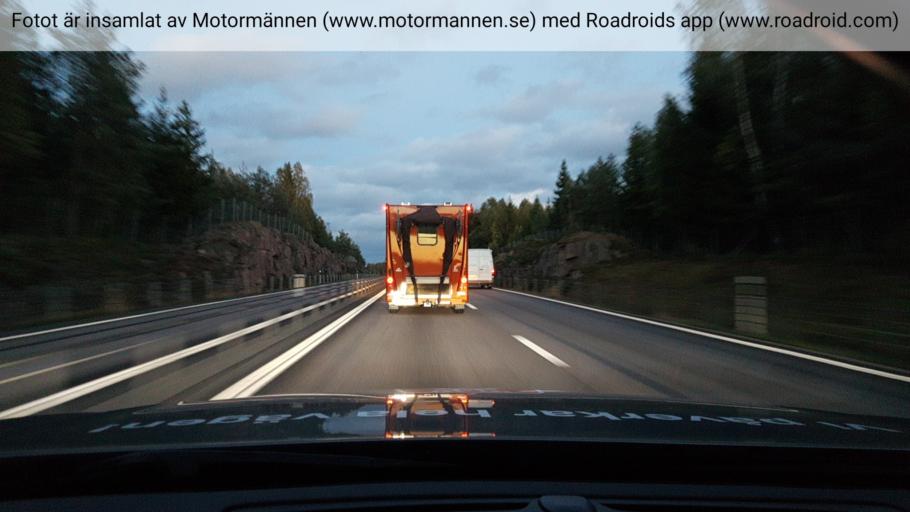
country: SE
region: Vaermland
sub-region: Karlstads Kommun
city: Skattkarr
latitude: 59.3932
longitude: 13.8243
